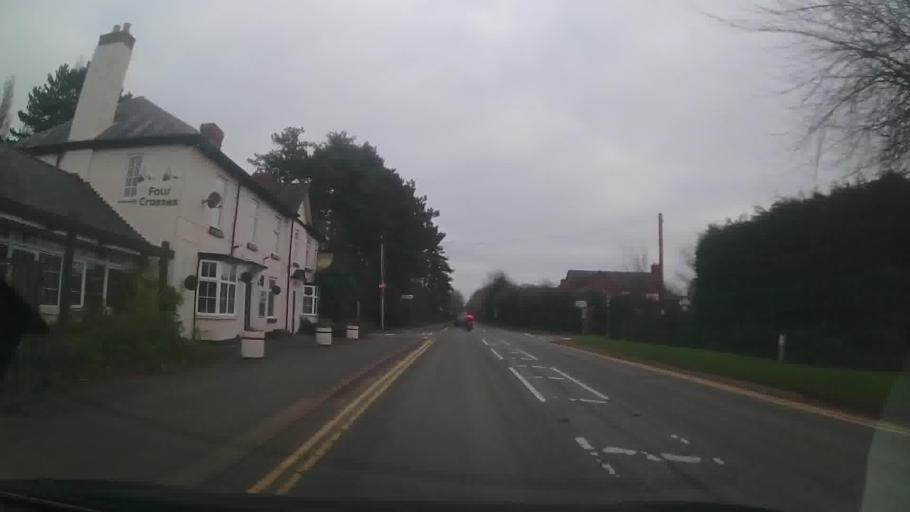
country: GB
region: England
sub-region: Shropshire
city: Bicton
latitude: 52.7236
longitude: -2.8091
